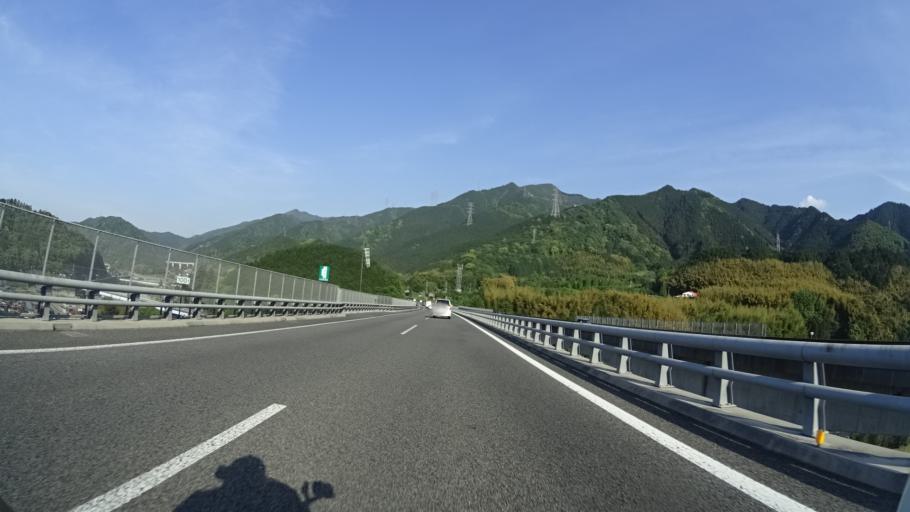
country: JP
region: Ehime
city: Saijo
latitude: 33.8857
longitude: 133.1794
